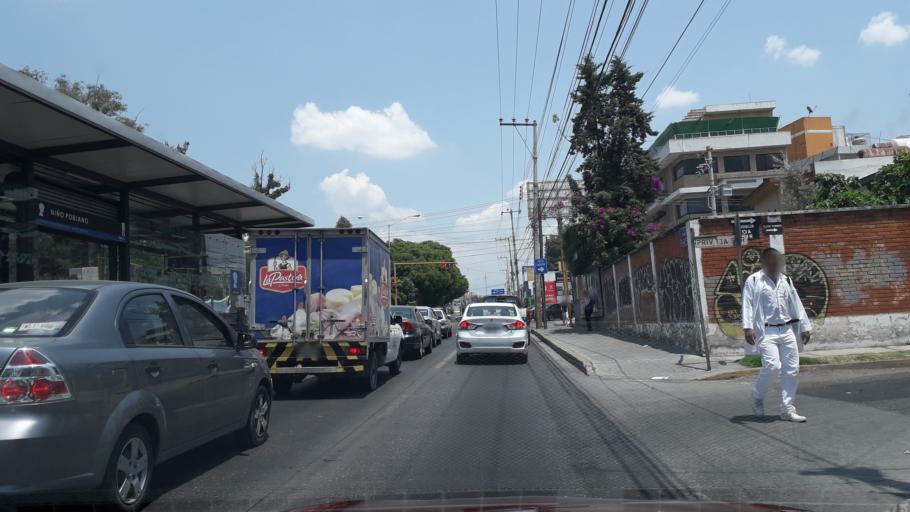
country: MX
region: Puebla
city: Puebla
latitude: 19.0257
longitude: -98.2220
